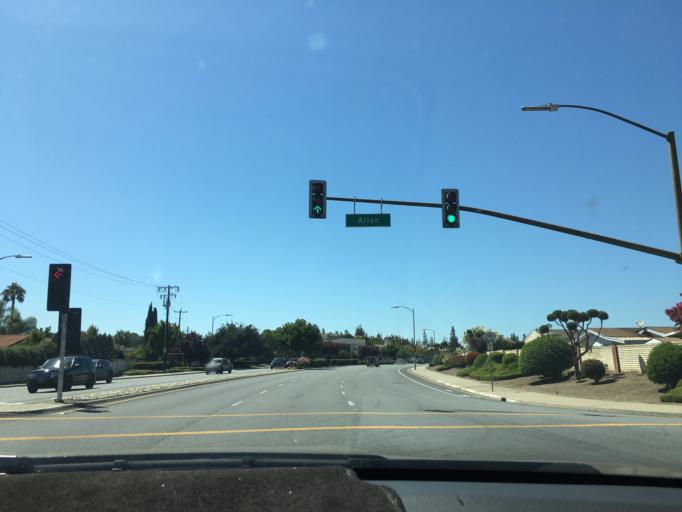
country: US
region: California
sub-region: Santa Clara County
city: Seven Trees
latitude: 37.2405
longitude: -121.8578
